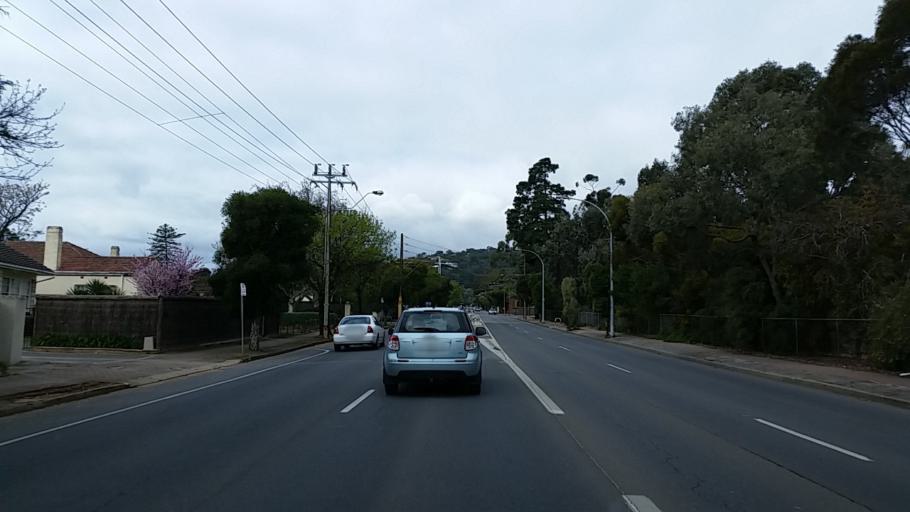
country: AU
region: South Australia
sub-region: Unley
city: Fullarton
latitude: -34.9642
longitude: 138.6338
